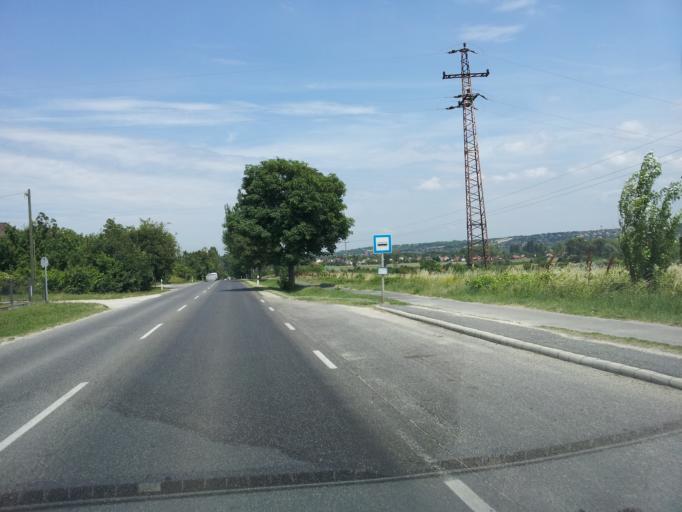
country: HU
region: Veszprem
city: Balatonalmadi
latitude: 47.0511
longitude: 18.0178
